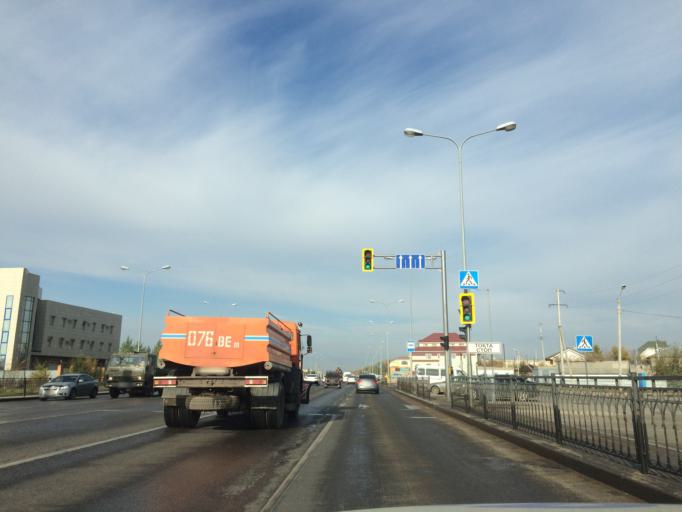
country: KZ
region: Astana Qalasy
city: Astana
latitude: 51.1767
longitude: 71.4748
